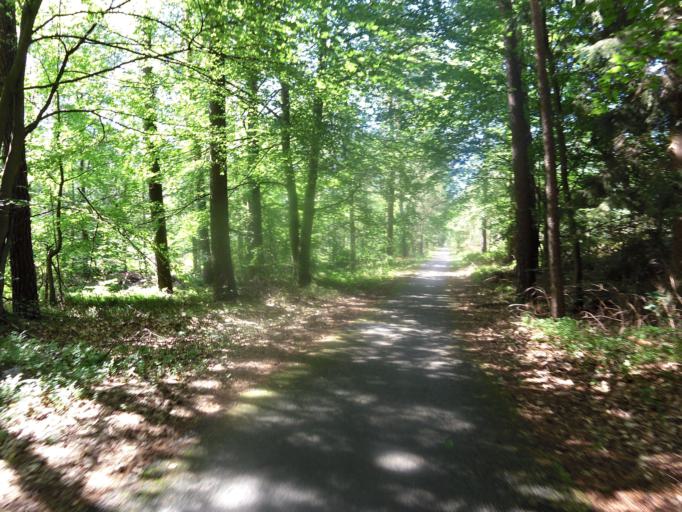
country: DE
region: Brandenburg
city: Lychen
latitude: 53.2007
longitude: 13.2584
